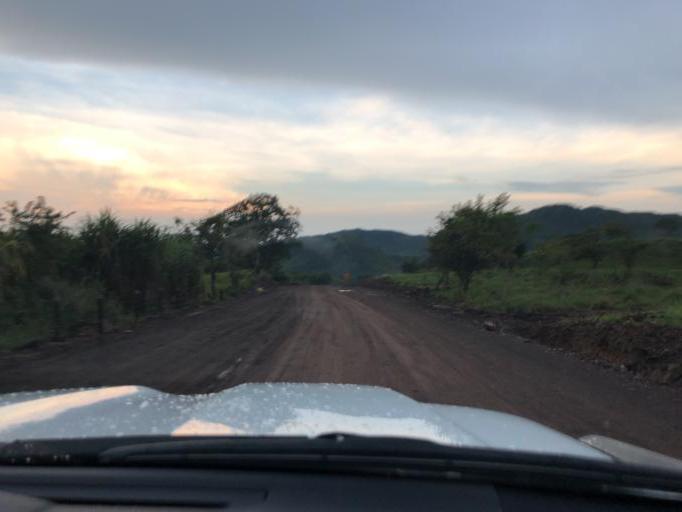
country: NI
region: Chontales
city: La Libertad
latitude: 12.1850
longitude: -85.1744
